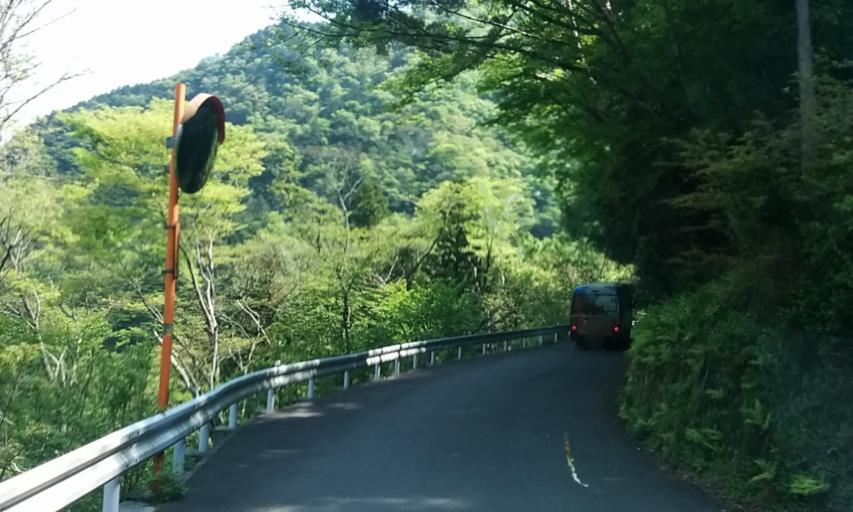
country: JP
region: Ehime
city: Niihama
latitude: 33.8710
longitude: 133.2949
